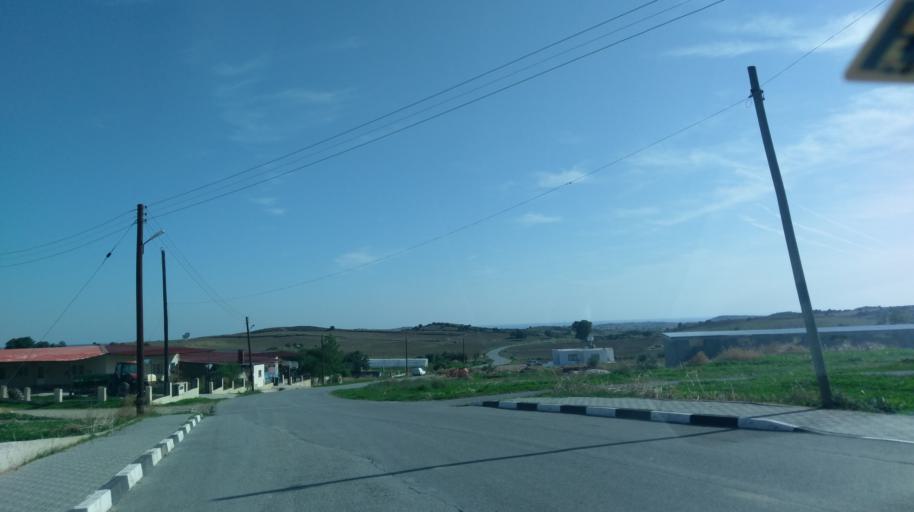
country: CY
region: Ammochostos
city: Trikomo
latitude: 35.3599
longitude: 33.9235
